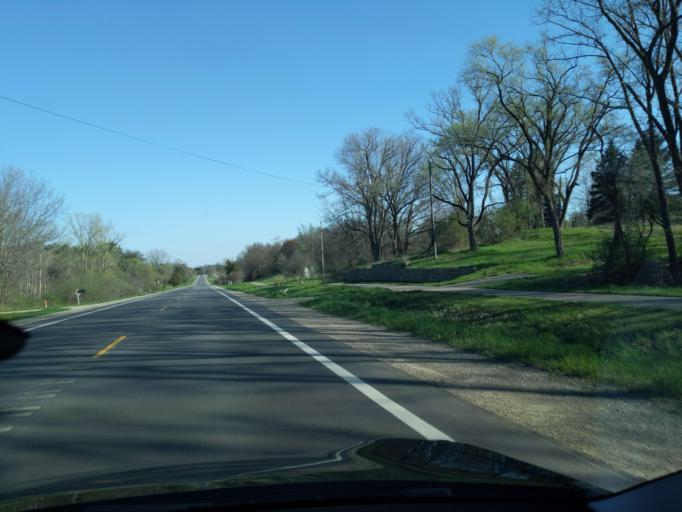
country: US
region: Michigan
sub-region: Washtenaw County
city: Chelsea
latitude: 42.3608
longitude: -84.0616
